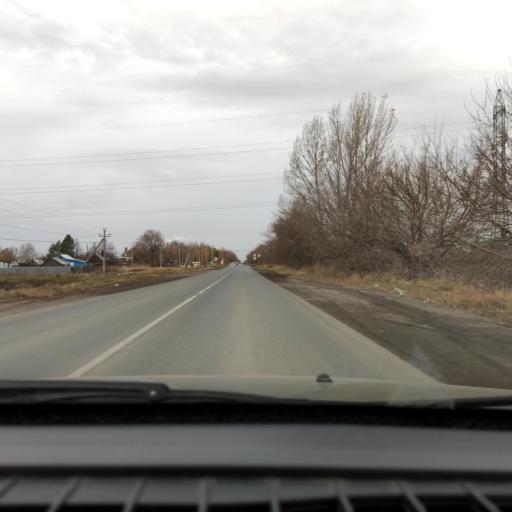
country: RU
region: Samara
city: Tol'yatti
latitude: 53.5751
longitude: 49.3314
